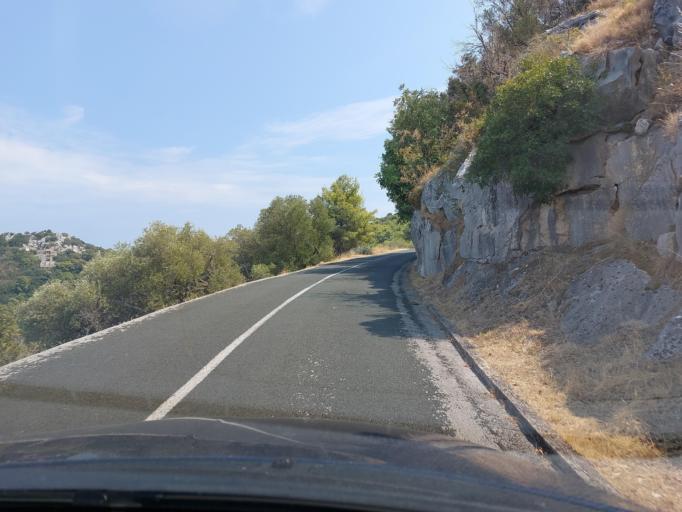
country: HR
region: Dubrovacko-Neretvanska
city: Smokvica
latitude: 42.7690
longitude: 16.8851
